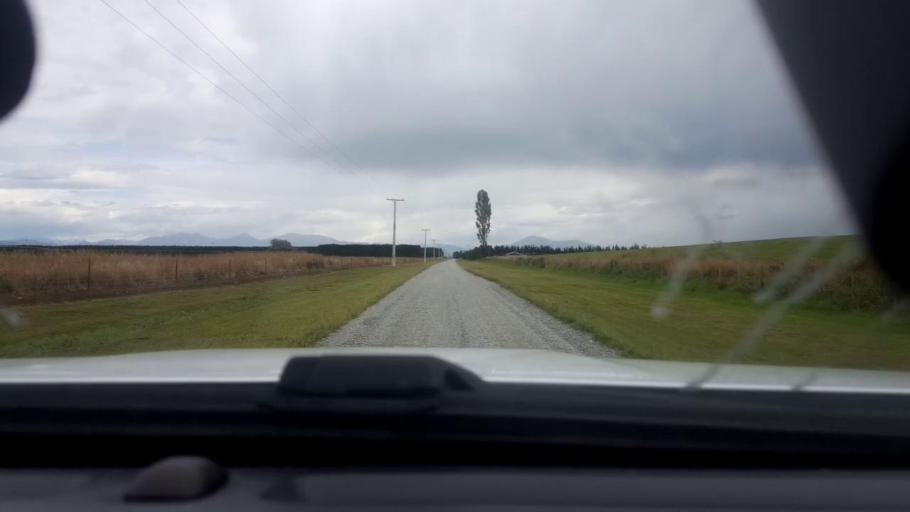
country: NZ
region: Canterbury
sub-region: Timaru District
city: Timaru
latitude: -44.1700
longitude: 171.4145
